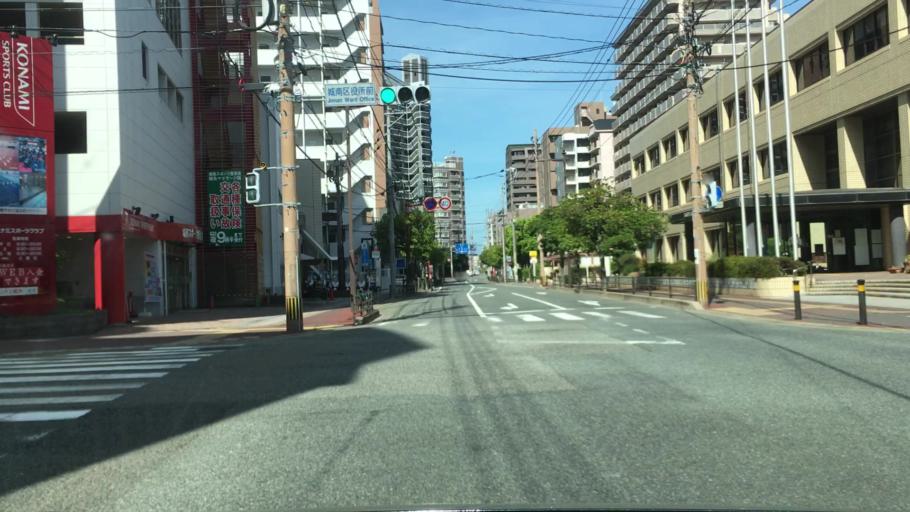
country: JP
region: Fukuoka
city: Fukuoka-shi
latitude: 33.5754
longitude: 130.3707
